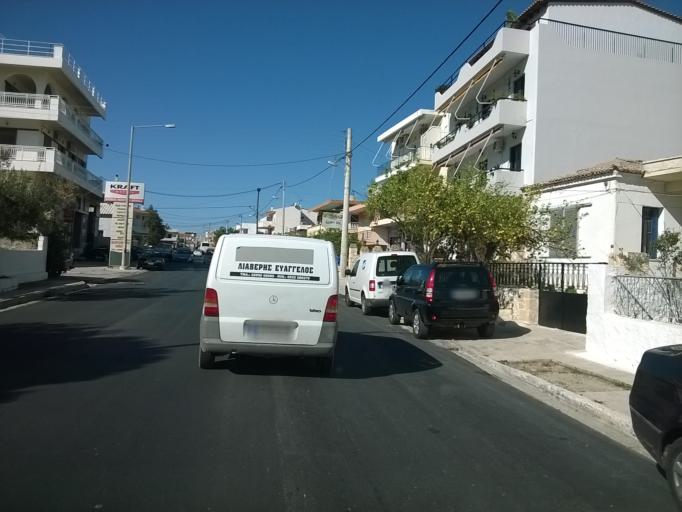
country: GR
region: Attica
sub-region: Nomarchia Anatolikis Attikis
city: Keratea
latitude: 37.8052
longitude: 23.9853
